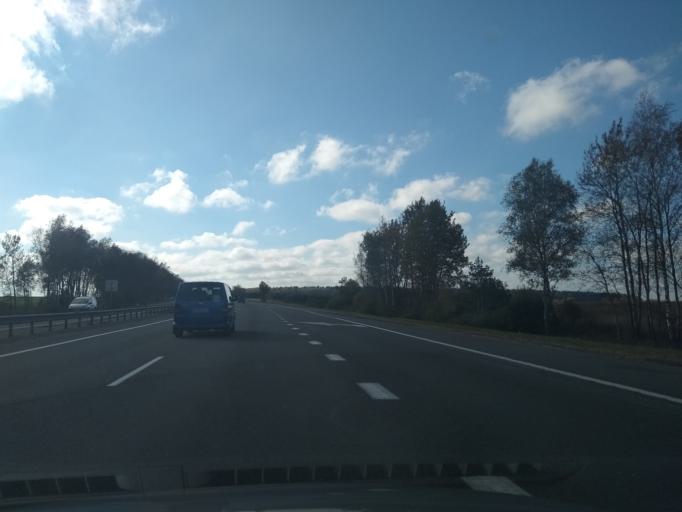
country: BY
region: Minsk
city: Enyerhyetykaw
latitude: 53.6500
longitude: 27.0734
